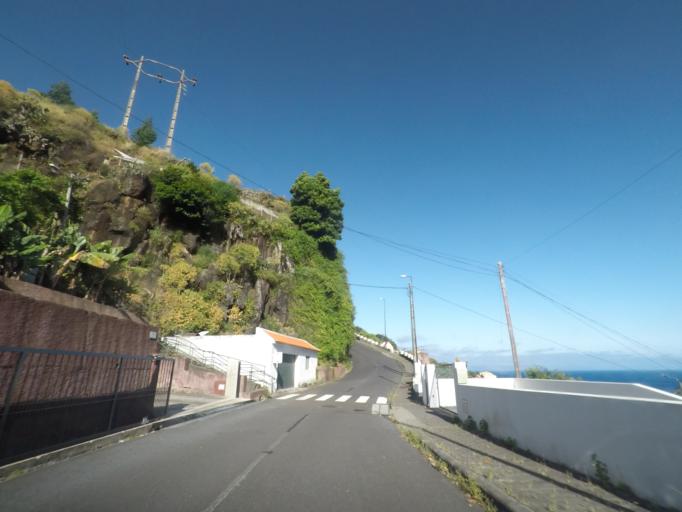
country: PT
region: Madeira
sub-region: Santa Cruz
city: Santa Cruz
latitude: 32.6927
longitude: -16.7995
